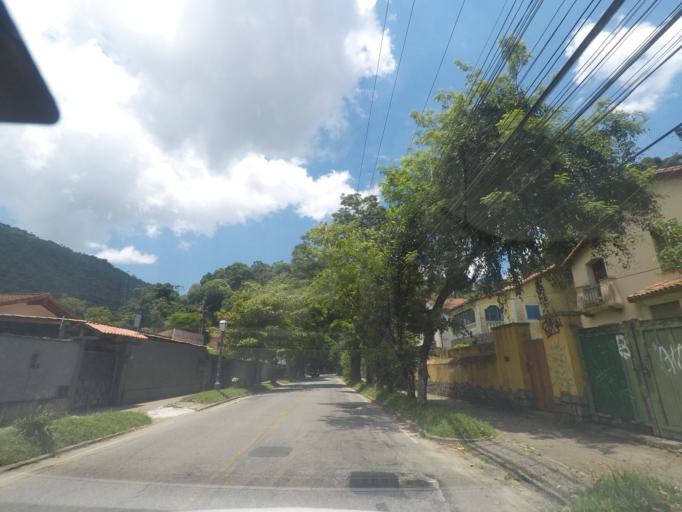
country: BR
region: Rio de Janeiro
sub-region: Petropolis
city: Petropolis
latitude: -22.5042
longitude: -43.1706
